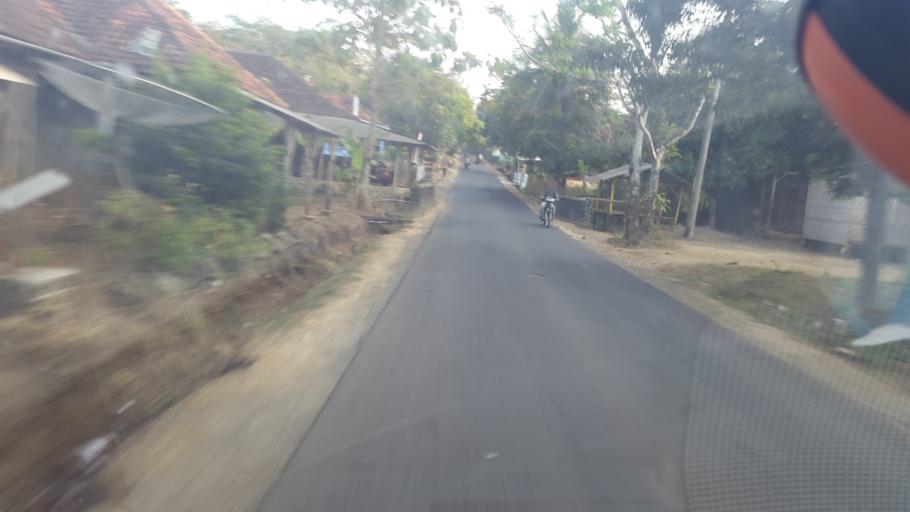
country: ID
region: West Java
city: Ciracap
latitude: -7.3392
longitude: 106.5267
